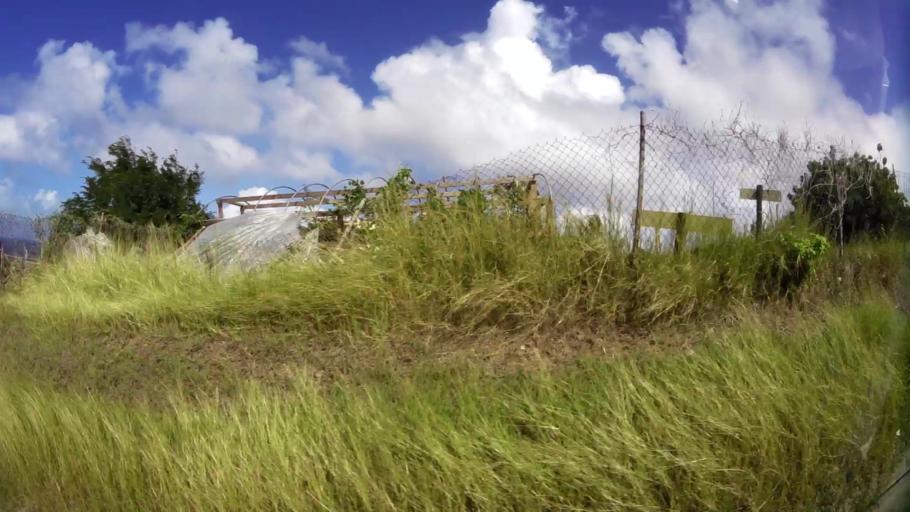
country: MS
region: Saint Peter
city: Brades
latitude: 16.7892
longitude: -62.2121
